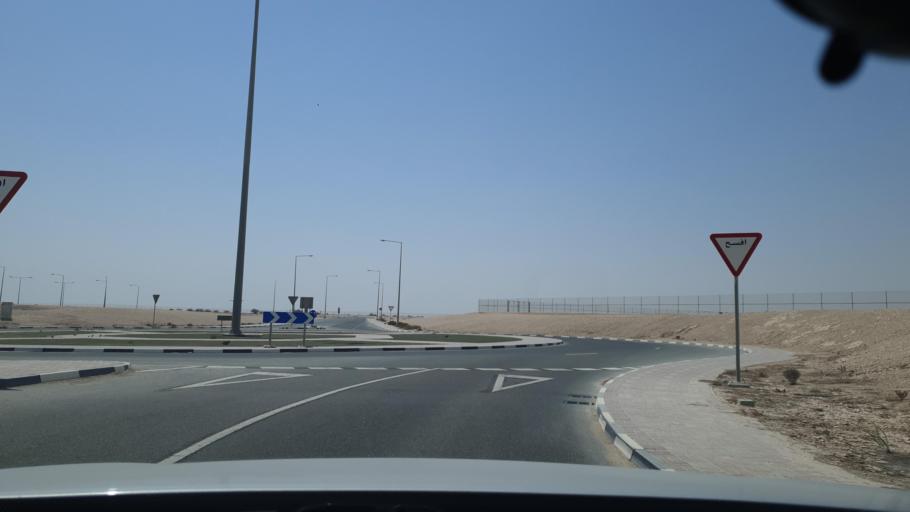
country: QA
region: Baladiyat ar Rayyan
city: Ar Rayyan
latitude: 25.3078
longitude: 51.3459
